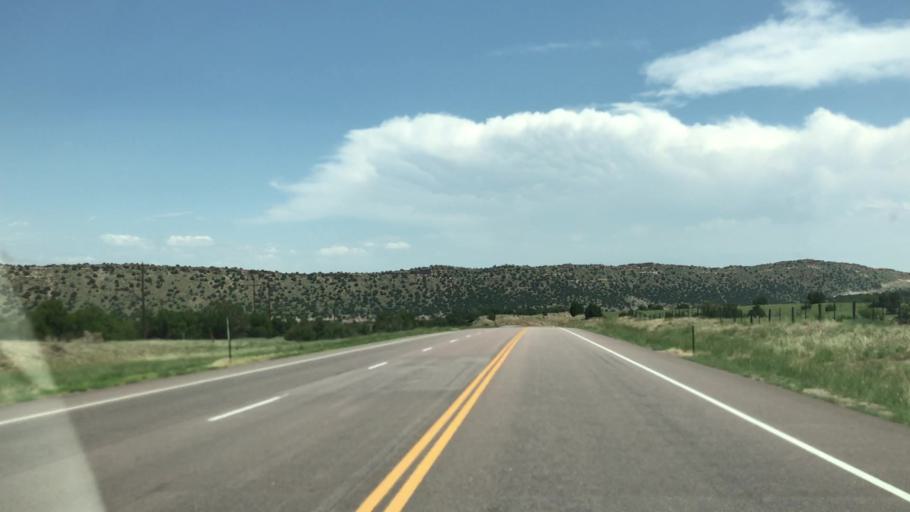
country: US
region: Colorado
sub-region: Fremont County
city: Canon City
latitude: 38.4849
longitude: -105.2708
